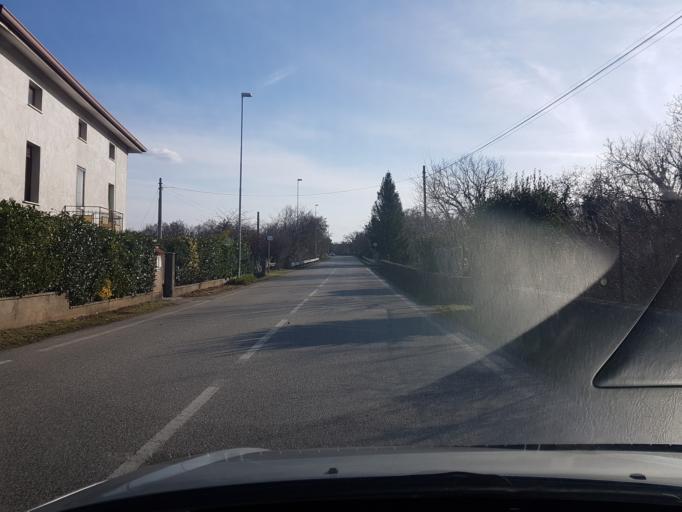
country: IT
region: Friuli Venezia Giulia
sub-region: Provincia di Trieste
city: Santa Croce
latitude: 45.7616
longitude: 13.7047
